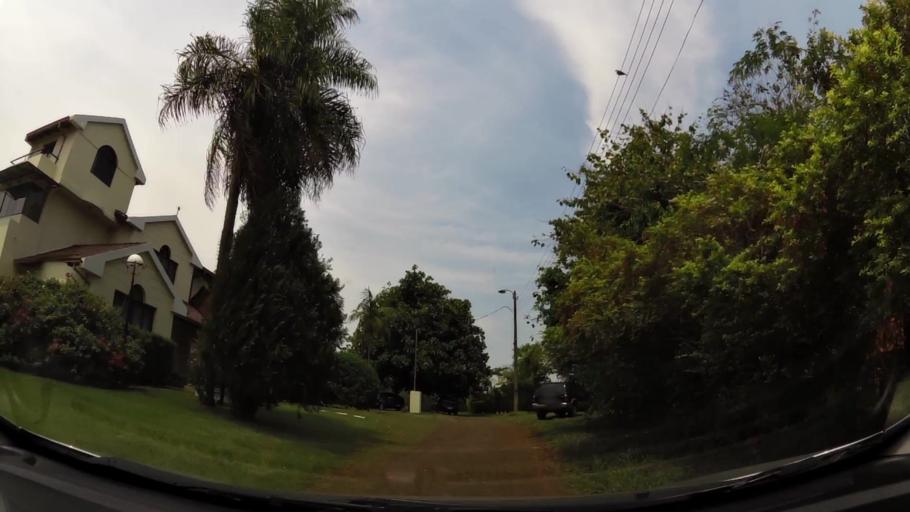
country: PY
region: Alto Parana
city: Ciudad del Este
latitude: -25.4969
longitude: -54.6083
